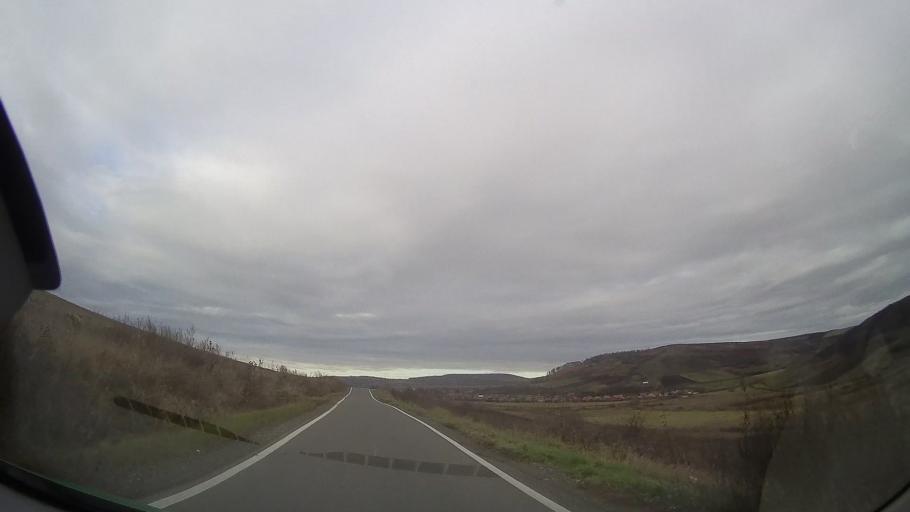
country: RO
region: Mures
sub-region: Comuna Faragau
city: Faragau
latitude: 46.7697
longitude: 24.5576
